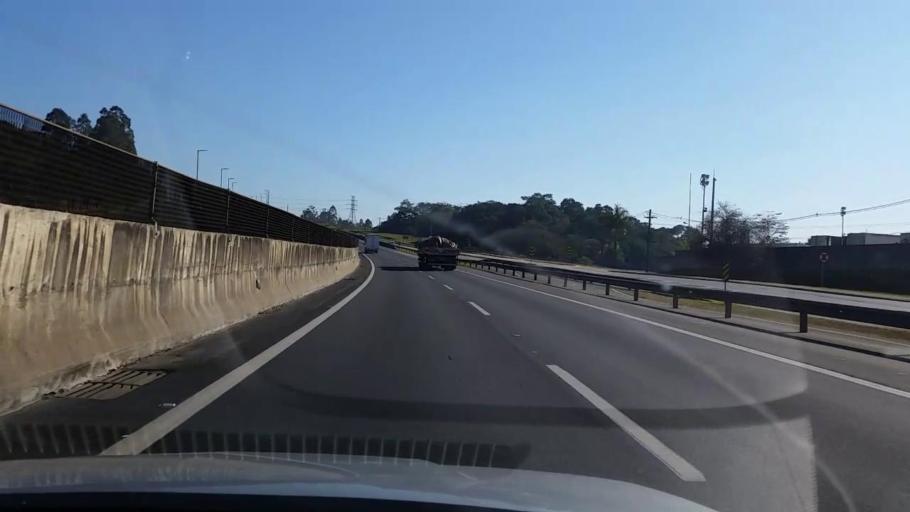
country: BR
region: Sao Paulo
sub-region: Varzea Paulista
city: Varzea Paulista
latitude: -23.2392
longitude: -46.8692
